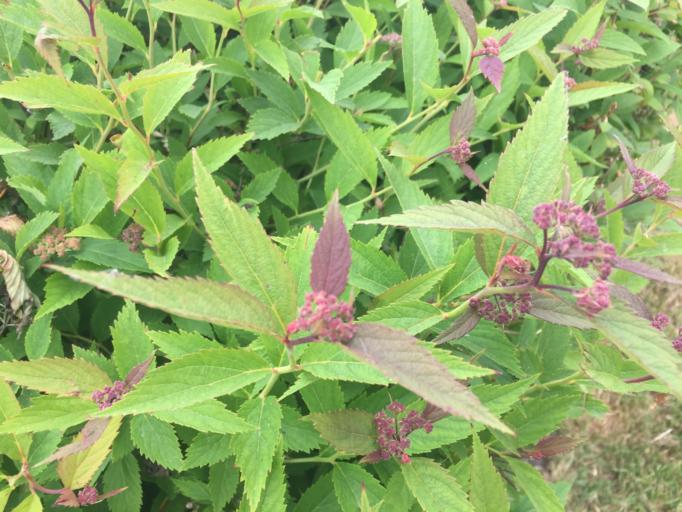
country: DK
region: South Denmark
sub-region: Middelfart Kommune
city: Norre Aby
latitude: 55.4594
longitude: 9.7980
